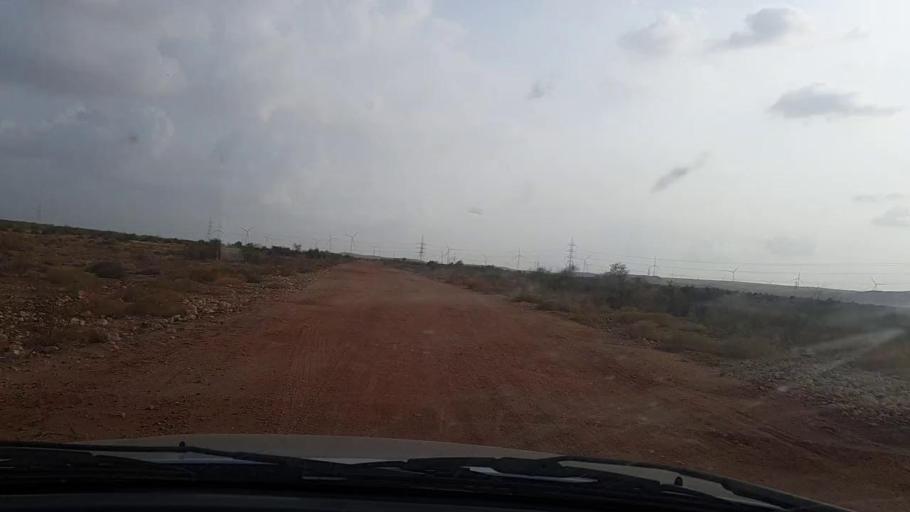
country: PK
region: Sindh
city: Thatta
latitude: 25.0660
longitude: 67.8880
